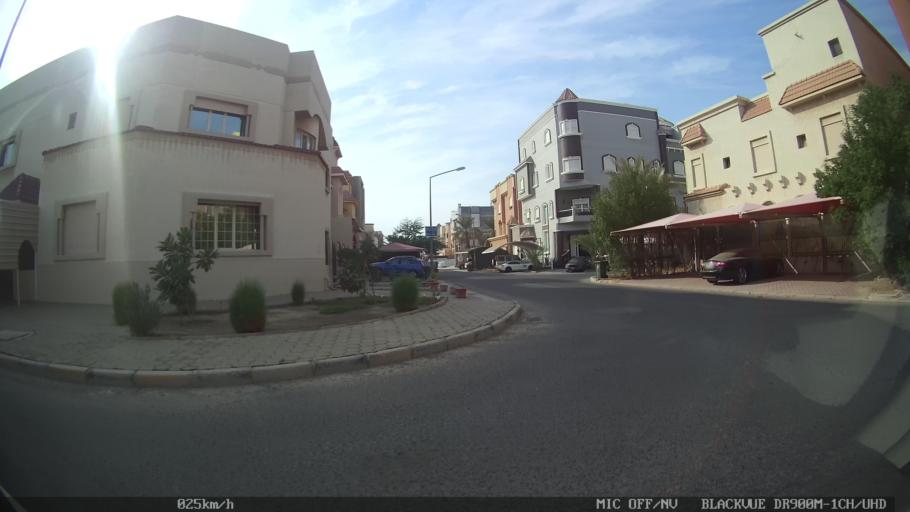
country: KW
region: Al Asimah
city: Ash Shamiyah
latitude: 29.3357
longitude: 47.9548
